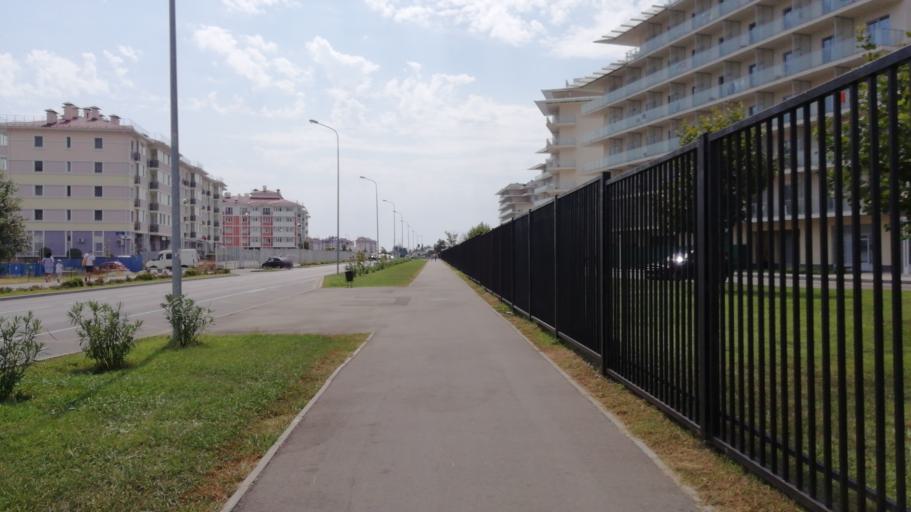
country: RU
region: Krasnodarskiy
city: Vysokoye
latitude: 43.4033
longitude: 39.9793
